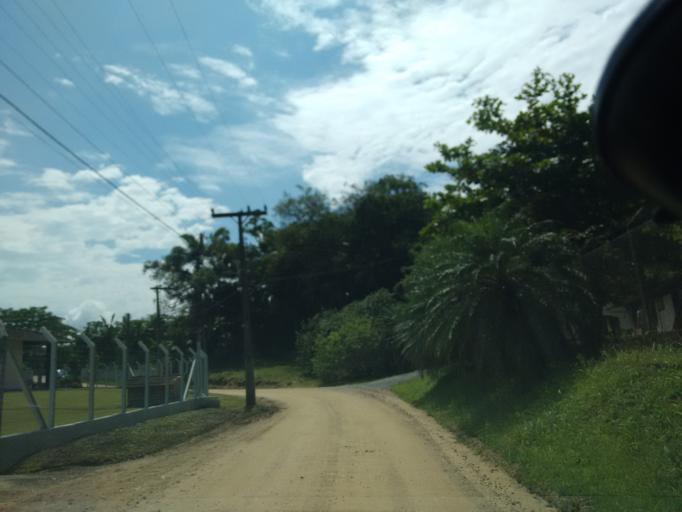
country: BR
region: Santa Catarina
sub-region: Indaial
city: Indaial
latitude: -26.8490
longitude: -49.1601
